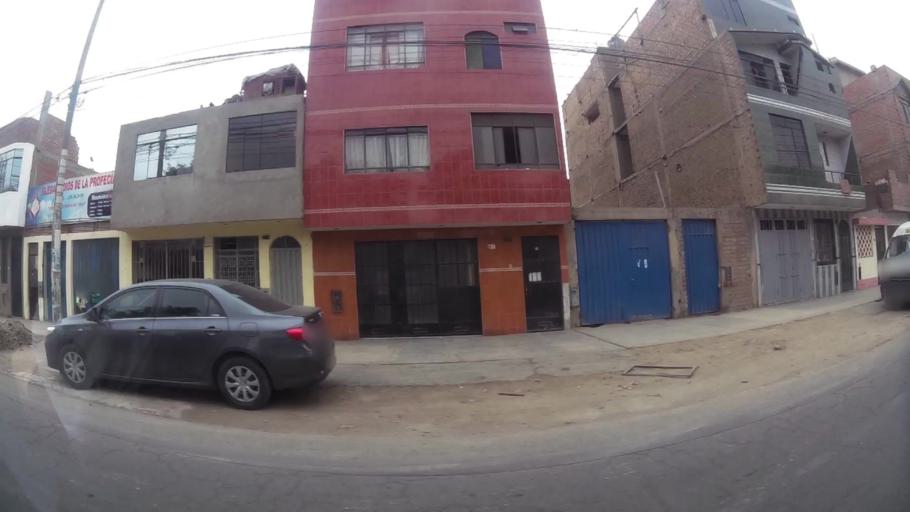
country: PE
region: Lima
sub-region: Lima
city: Independencia
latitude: -11.9571
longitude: -77.0758
